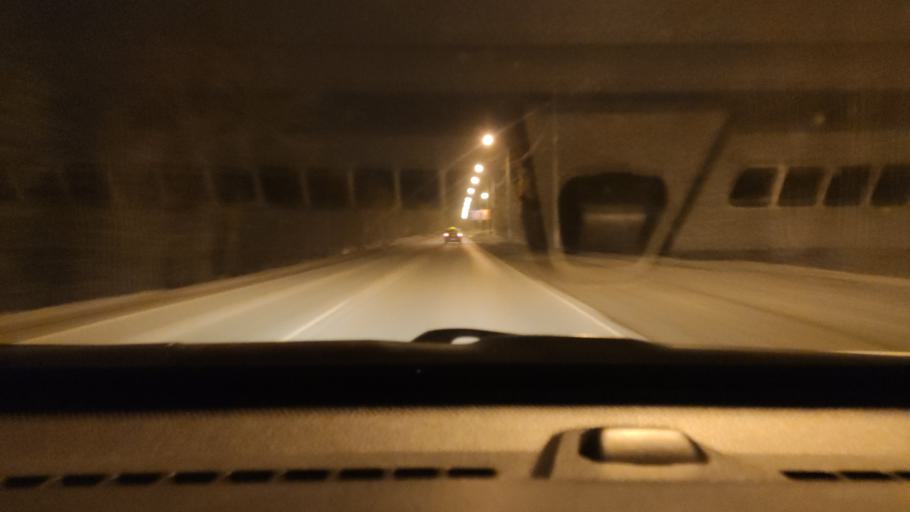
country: RU
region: Samara
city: Tol'yatti
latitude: 53.4745
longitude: 49.4086
